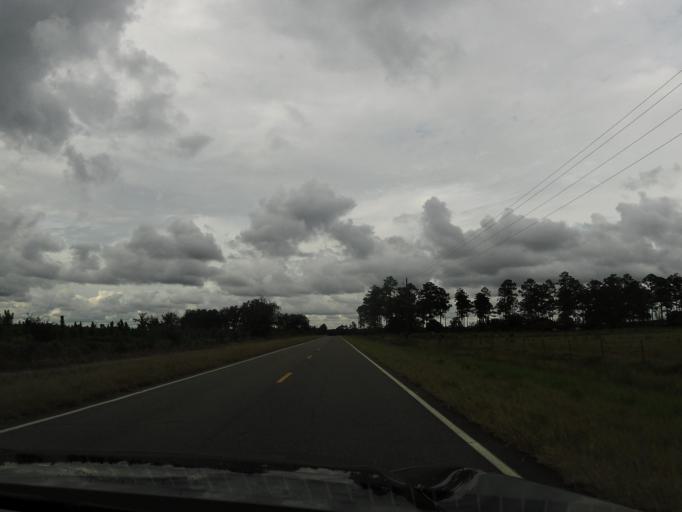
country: US
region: Florida
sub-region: Baker County
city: Macclenny
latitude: 30.4320
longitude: -82.1982
